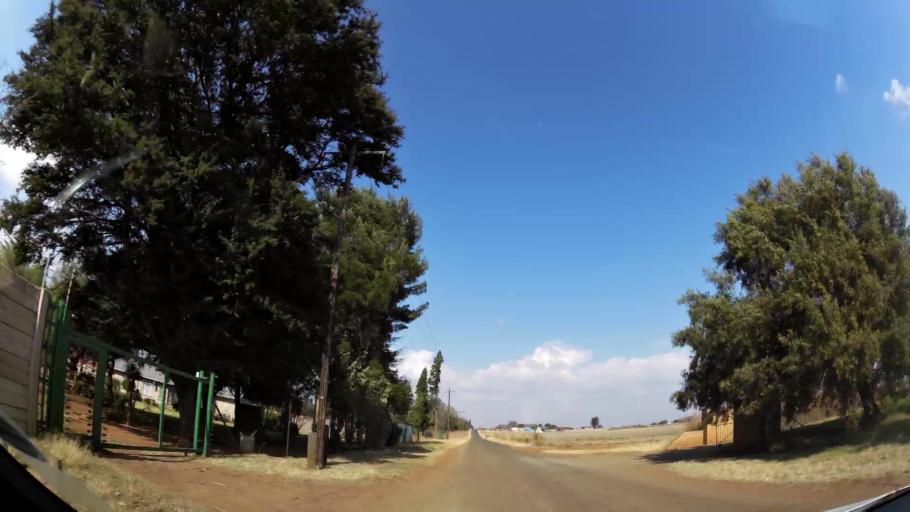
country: ZA
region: Gauteng
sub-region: Ekurhuleni Metropolitan Municipality
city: Springs
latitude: -26.1818
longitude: 28.5337
